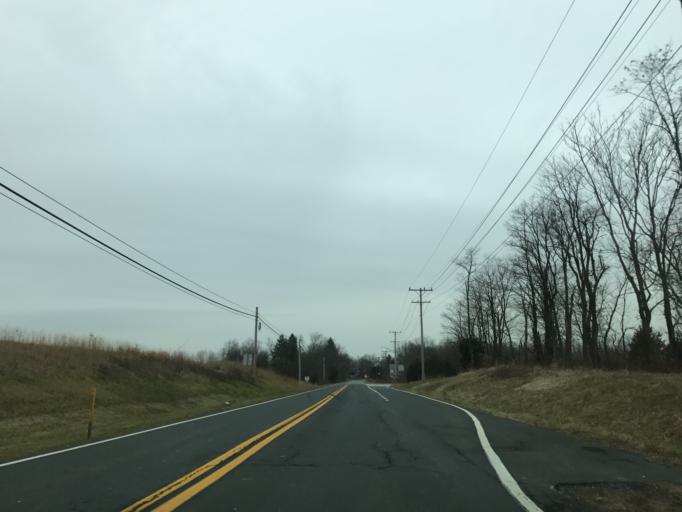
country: US
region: Maryland
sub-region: Carroll County
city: Taneytown
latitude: 39.6439
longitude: -77.1651
